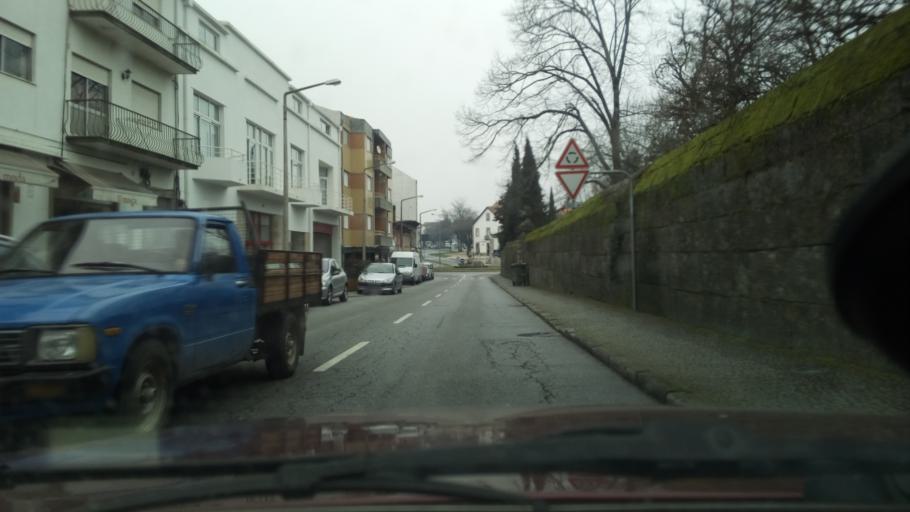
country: PT
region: Viseu
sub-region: Mangualde
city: Mangualde
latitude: 40.6051
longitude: -7.7639
